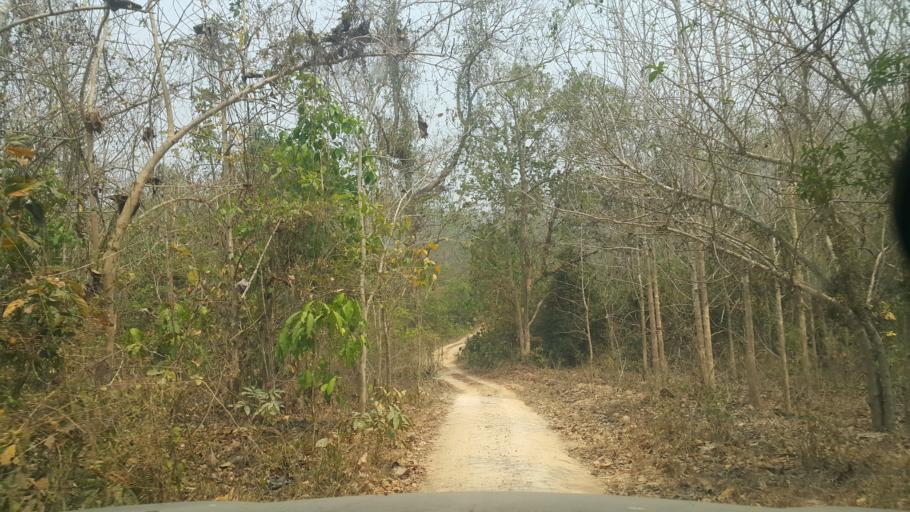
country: TH
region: Lampang
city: Hang Chat
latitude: 18.3204
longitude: 99.2463
